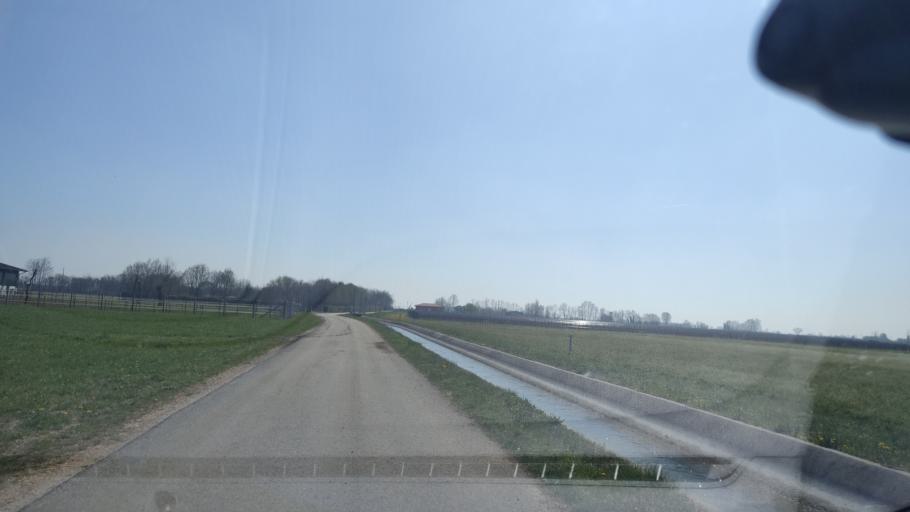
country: IT
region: Friuli Venezia Giulia
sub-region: Provincia di Pordenone
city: Budoia
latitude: 46.0204
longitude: 12.5454
